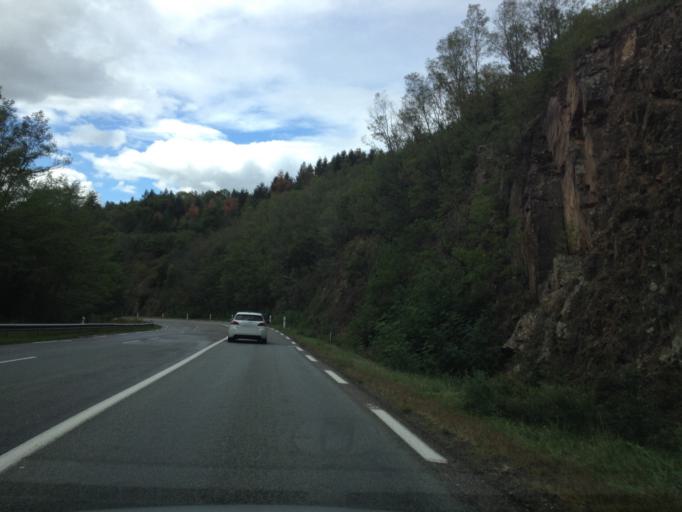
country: FR
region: Rhone-Alpes
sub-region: Departement de la Loire
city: Saint-Symphorien-de-Lay
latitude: 45.9664
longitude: 4.1504
